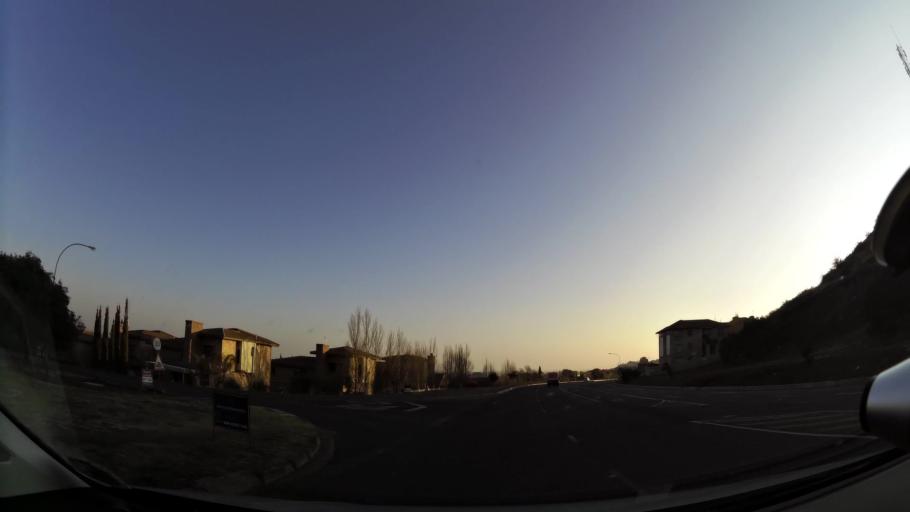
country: ZA
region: Orange Free State
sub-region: Mangaung Metropolitan Municipality
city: Bloemfontein
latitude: -29.0889
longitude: 26.1640
